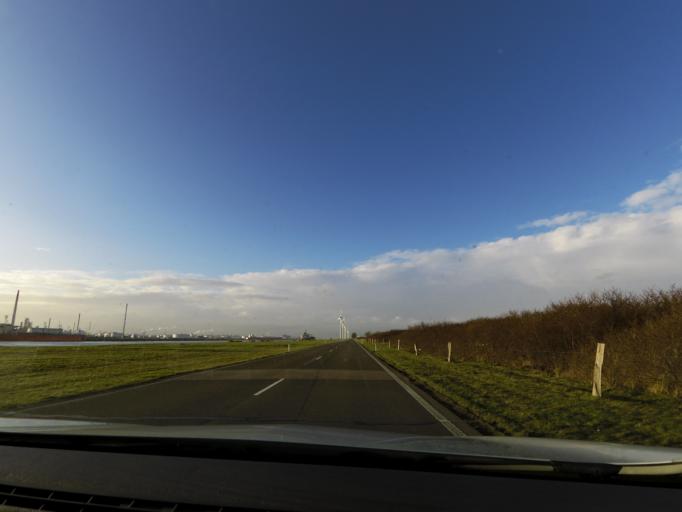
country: NL
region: South Holland
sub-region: Gemeente Westland
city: Maasdijk
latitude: 51.9360
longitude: 4.1932
